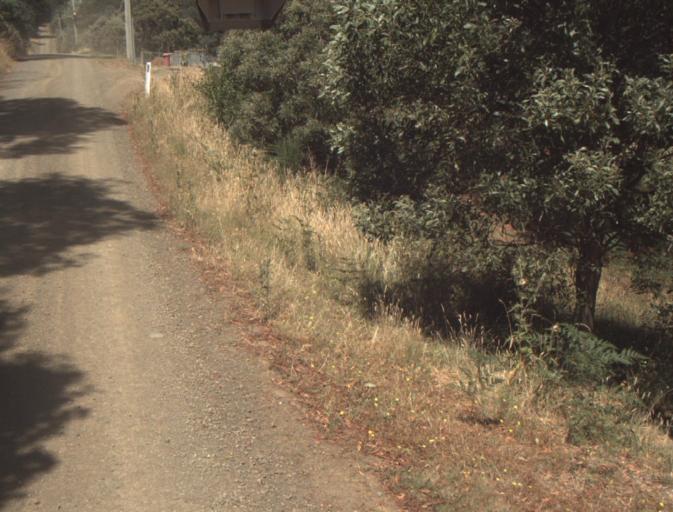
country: AU
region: Tasmania
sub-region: Launceston
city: Newstead
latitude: -41.3515
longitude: 147.3788
